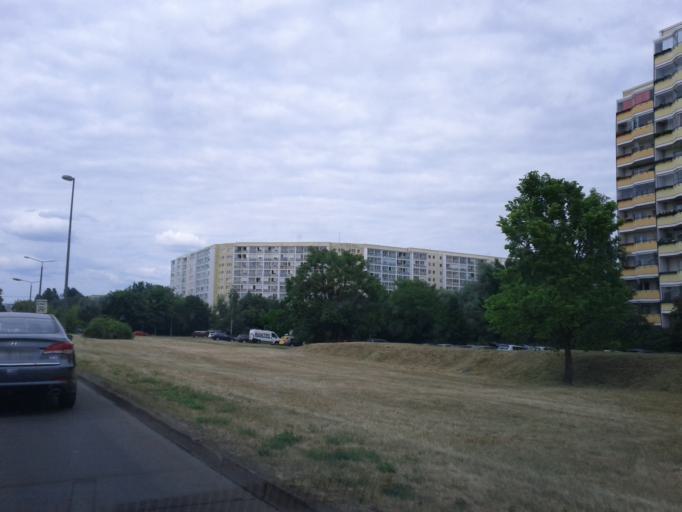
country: DE
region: Berlin
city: Marzahn
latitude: 52.5485
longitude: 13.5722
